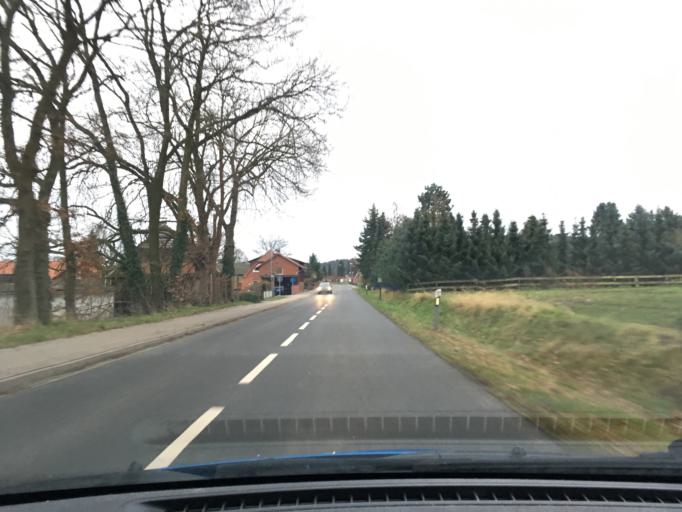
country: DE
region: Lower Saxony
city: Tosterglope
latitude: 53.2409
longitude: 10.8411
